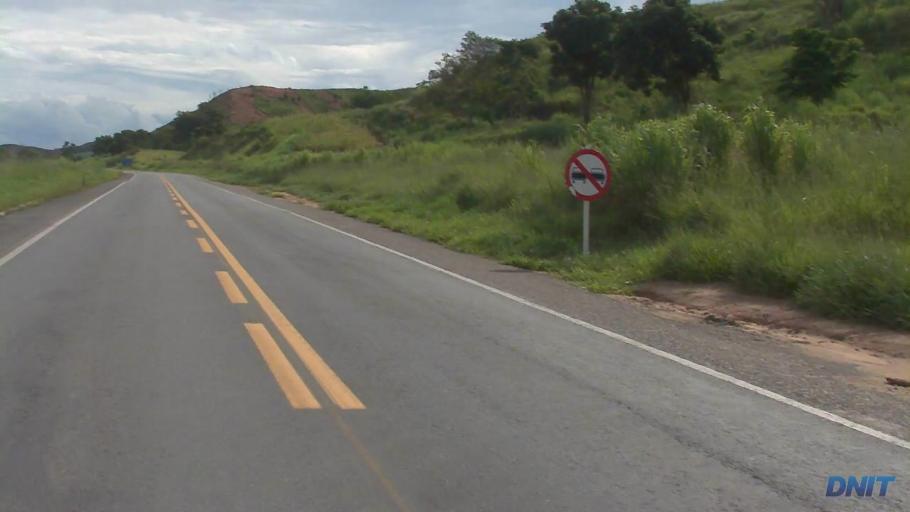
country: BR
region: Minas Gerais
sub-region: Belo Oriente
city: Belo Oriente
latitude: -19.1898
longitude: -42.2717
